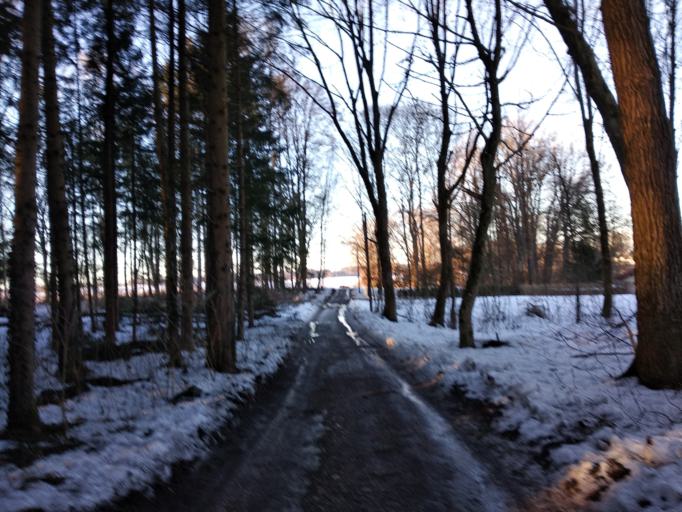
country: DE
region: Bavaria
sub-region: Upper Bavaria
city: Grafing bei Munchen
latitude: 48.0447
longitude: 11.9511
